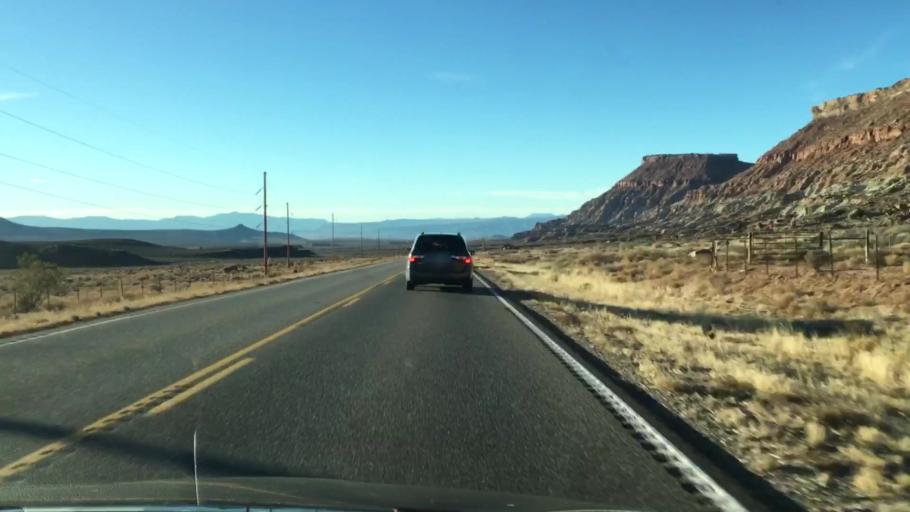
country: US
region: Utah
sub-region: Washington County
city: LaVerkin
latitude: 37.1232
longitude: -113.1944
